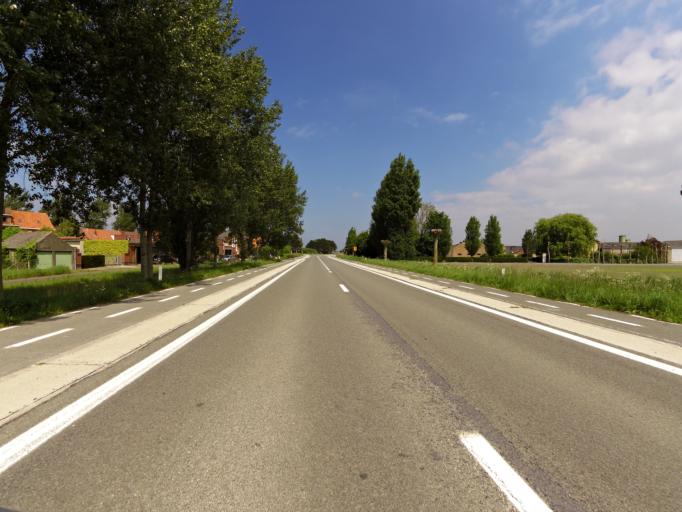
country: BE
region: Flanders
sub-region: Provincie West-Vlaanderen
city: Veurne
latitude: 51.1049
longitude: 2.7033
